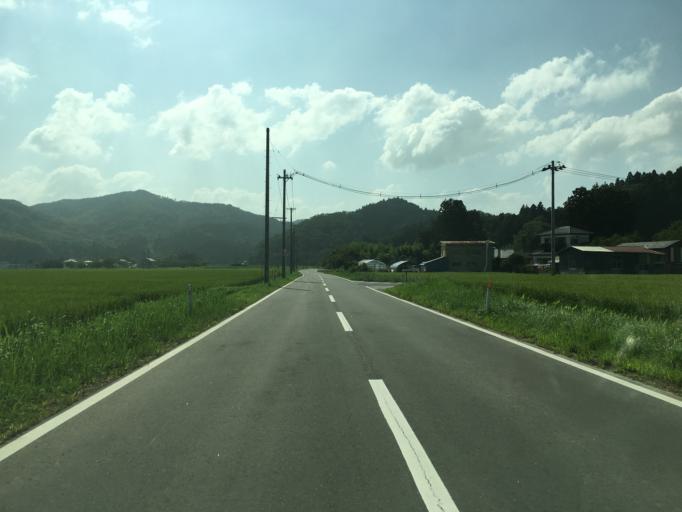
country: JP
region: Miyagi
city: Marumori
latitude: 37.8928
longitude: 140.8173
